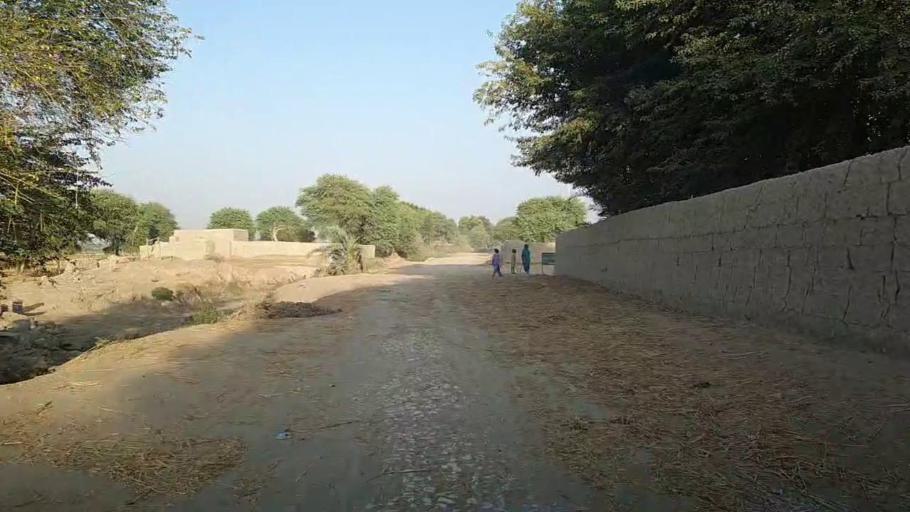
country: PK
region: Sindh
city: Kashmor
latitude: 28.4283
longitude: 69.4570
